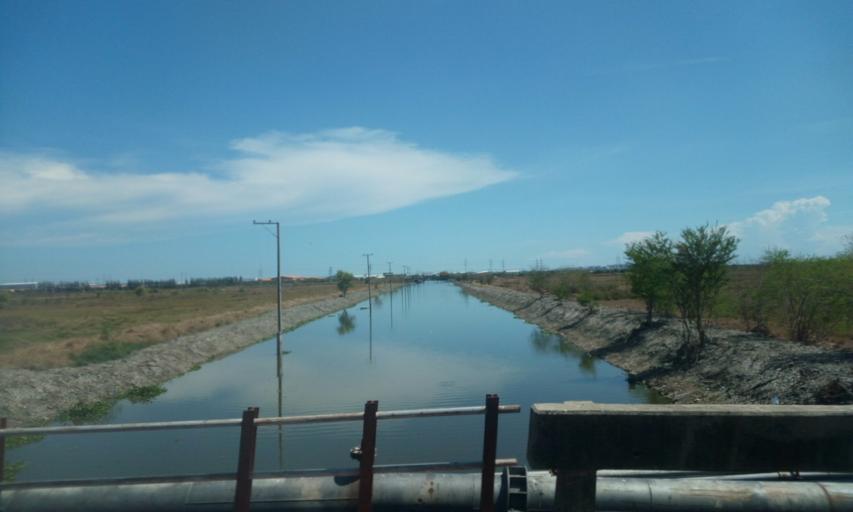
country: TH
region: Samut Prakan
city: Bang Bo District
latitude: 13.5591
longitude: 100.7825
